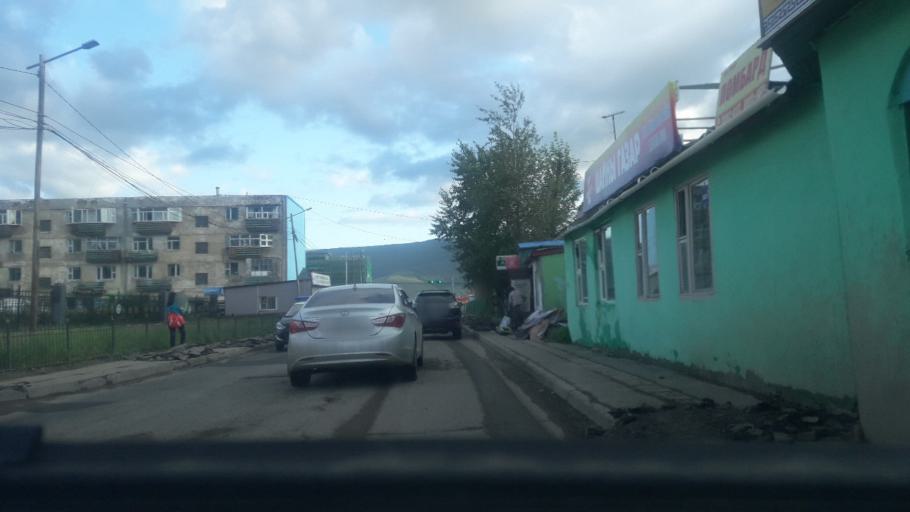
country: MN
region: Ulaanbaatar
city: Ulaanbaatar
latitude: 47.9143
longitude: 106.9947
